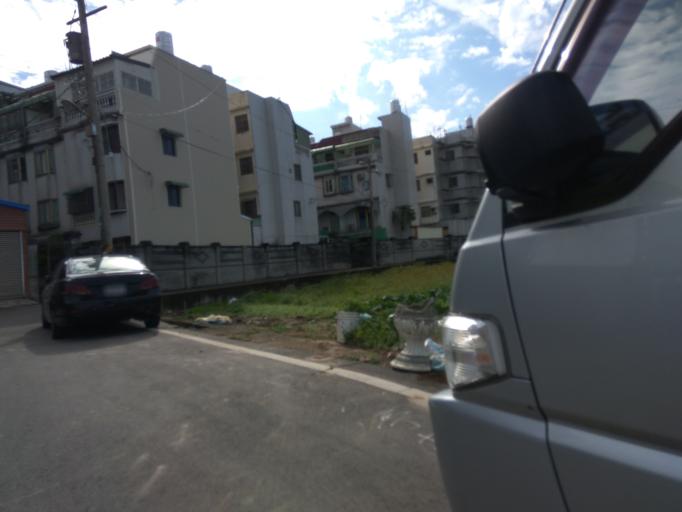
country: TW
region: Taiwan
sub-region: Hsinchu
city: Zhubei
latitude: 24.9878
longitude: 121.0932
